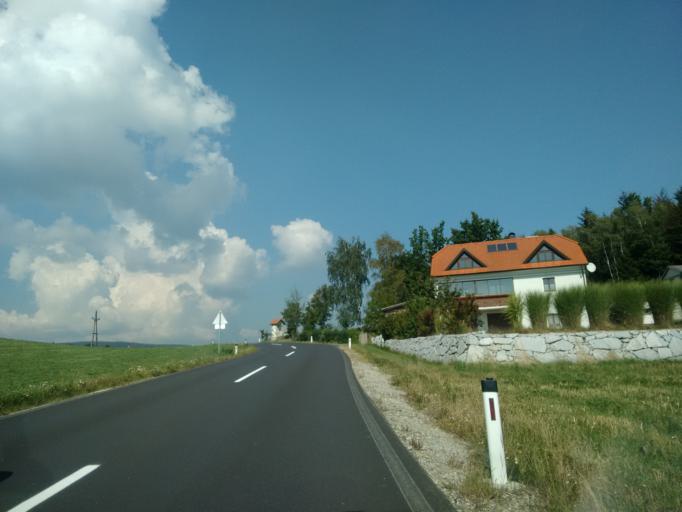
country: AT
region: Upper Austria
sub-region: Politischer Bezirk Urfahr-Umgebung
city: Altenberg bei Linz
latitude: 48.3961
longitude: 14.3462
